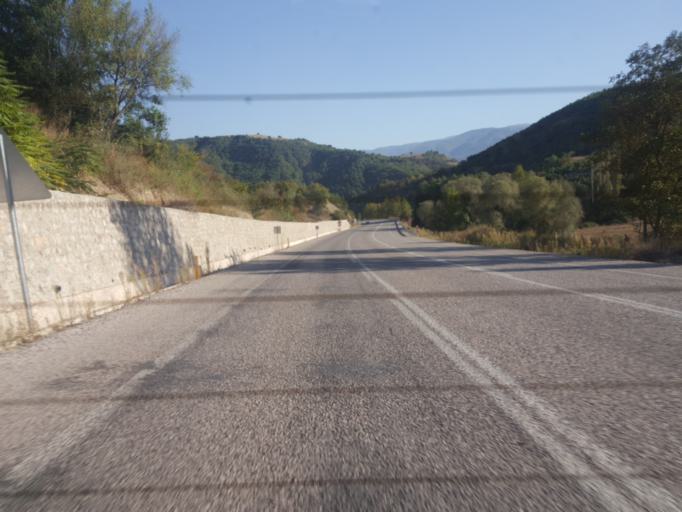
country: TR
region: Amasya
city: Tasova
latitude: 40.7575
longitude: 36.2860
